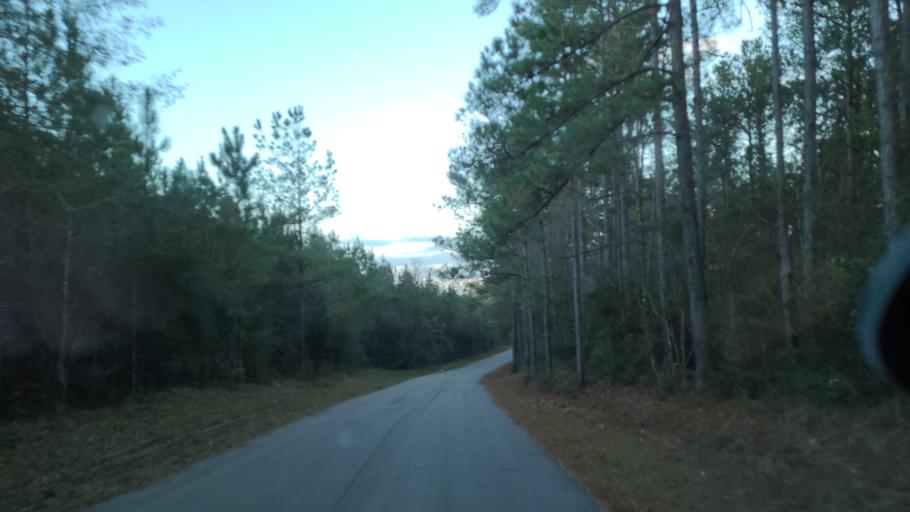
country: US
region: Mississippi
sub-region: Perry County
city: New Augusta
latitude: 31.1338
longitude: -89.2053
